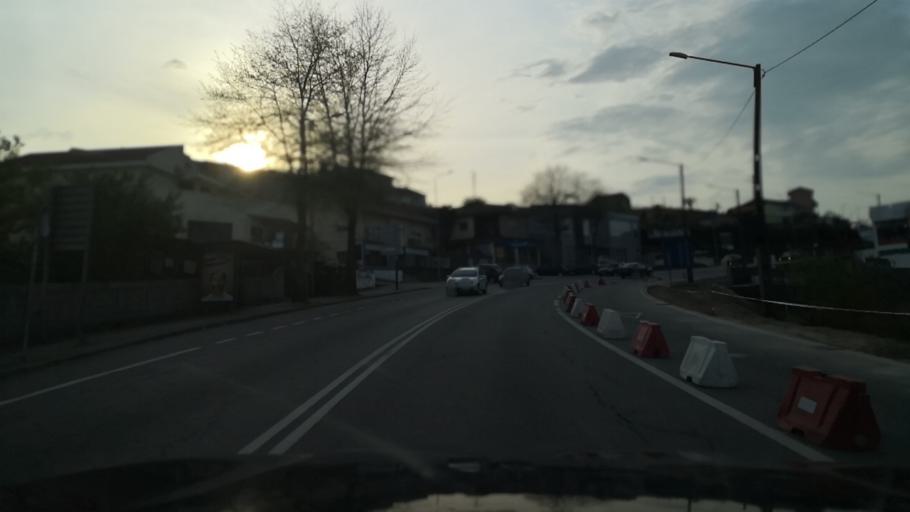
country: PT
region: Porto
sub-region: Valongo
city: Valongo
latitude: 41.1902
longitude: -8.5055
